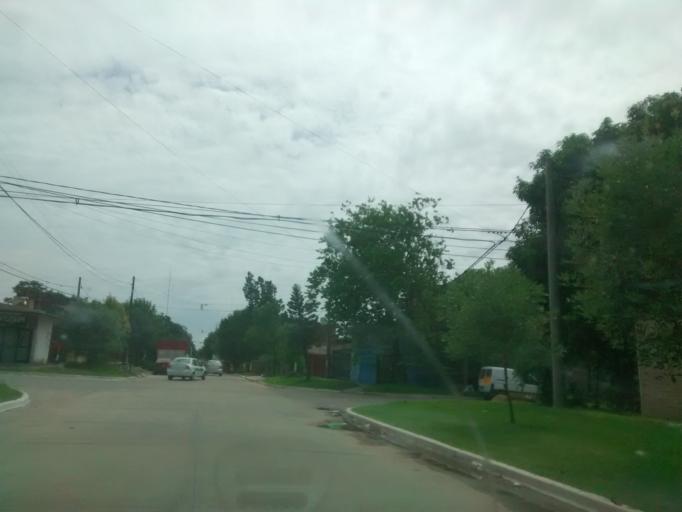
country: AR
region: Chaco
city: Resistencia
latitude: -27.4425
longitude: -59.0020
